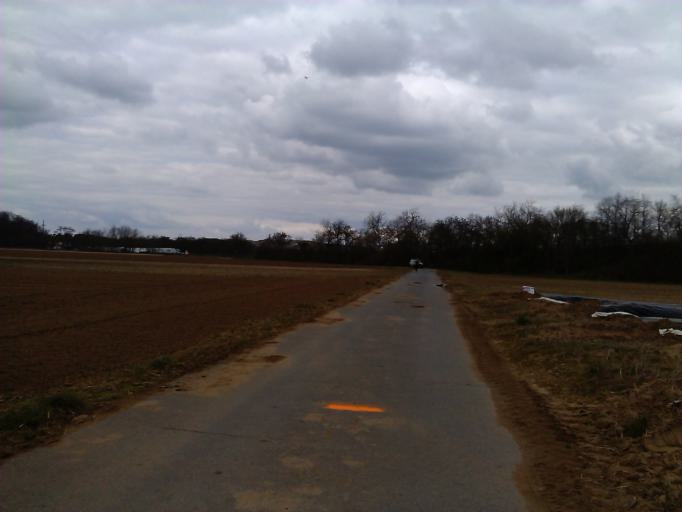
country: DE
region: Hesse
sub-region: Regierungsbezirk Darmstadt
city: Buttelborn
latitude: 49.8885
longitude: 8.5489
